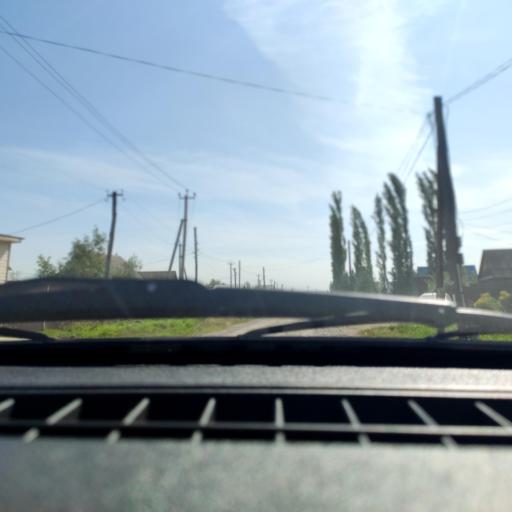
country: RU
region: Bashkortostan
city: Iglino
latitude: 54.8508
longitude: 56.4254
